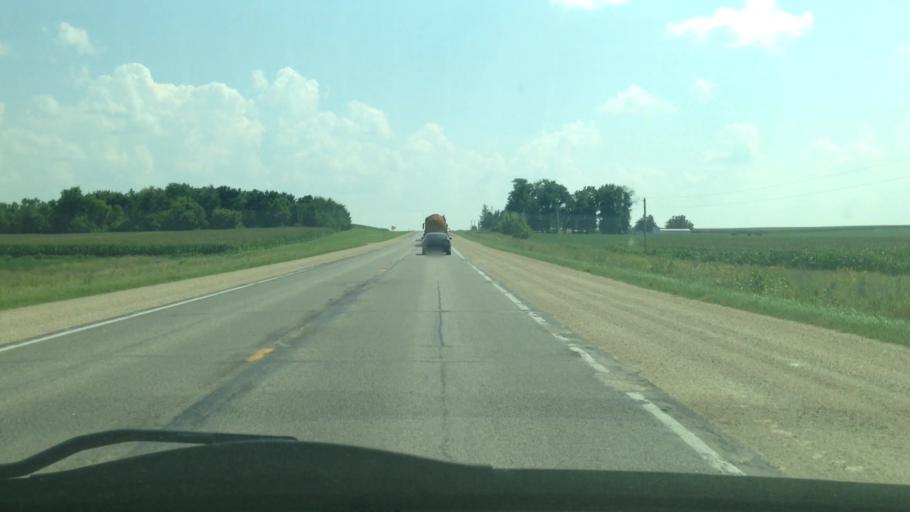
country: US
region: Iowa
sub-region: Chickasaw County
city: New Hampton
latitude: 43.2251
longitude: -92.2985
